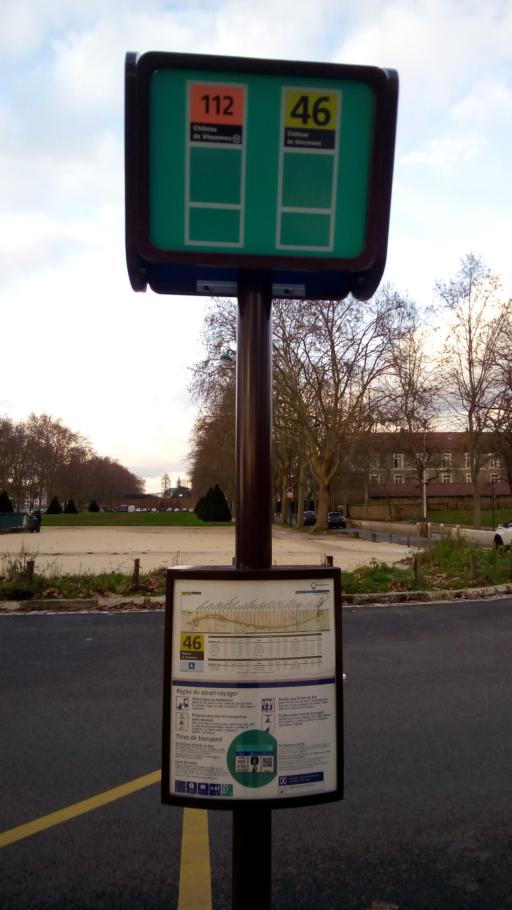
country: FR
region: Ile-de-France
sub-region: Departement du Val-de-Marne
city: Vincennes
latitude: 48.8404
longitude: 2.4384
